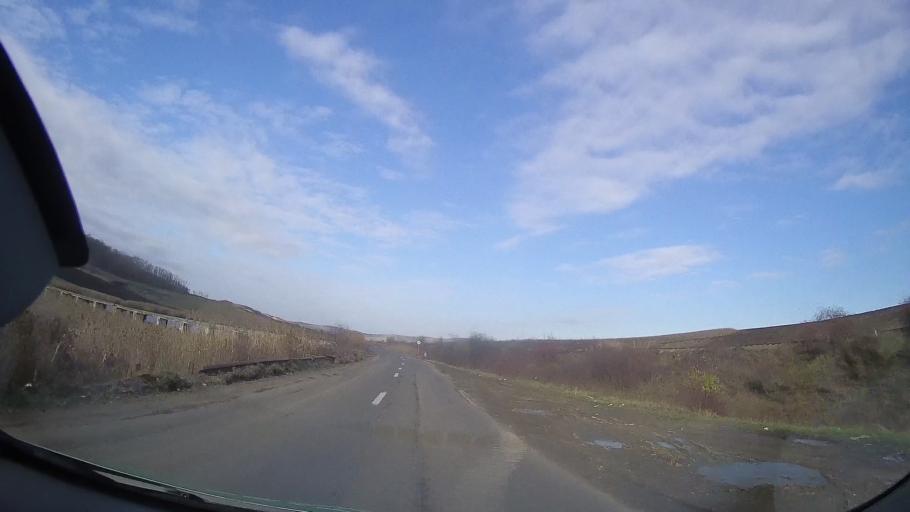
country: RO
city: Barza
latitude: 46.5562
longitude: 24.1000
